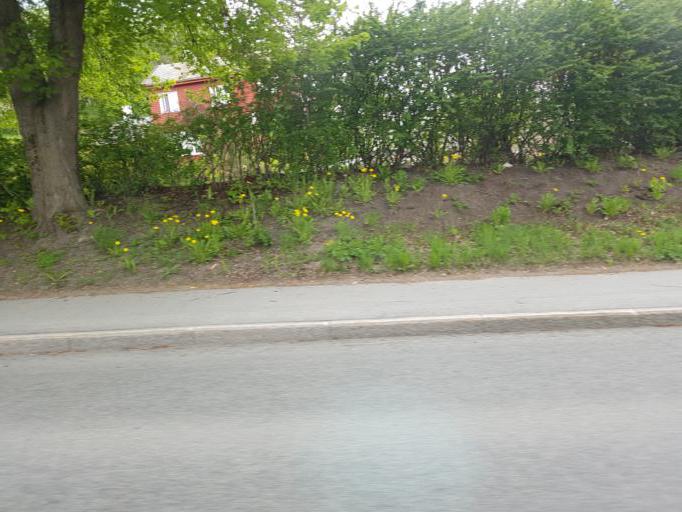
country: NO
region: Nord-Trondelag
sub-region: Levanger
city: Levanger
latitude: 63.7470
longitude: 11.2790
